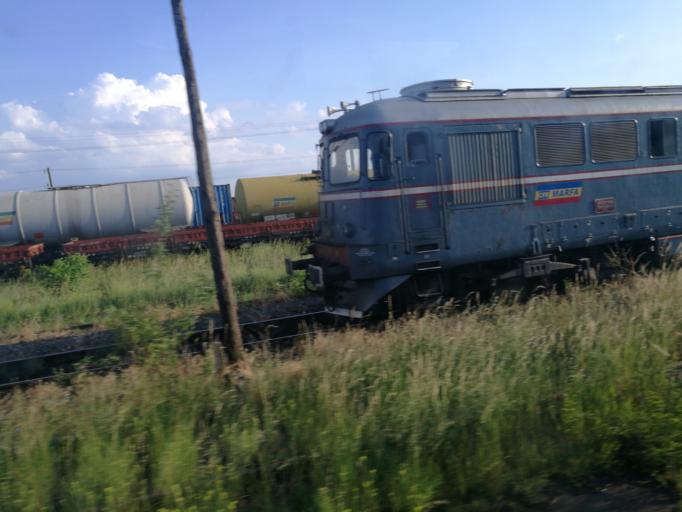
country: RO
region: Arges
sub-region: Oras Stefanesti
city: Golesti
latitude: 44.8362
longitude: 24.9673
